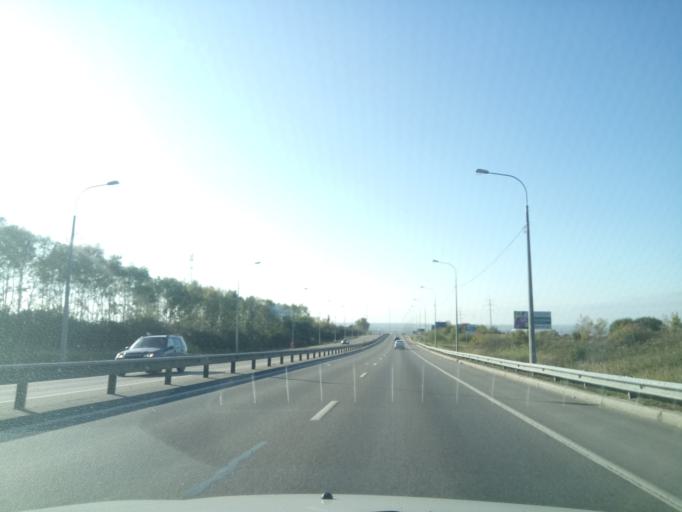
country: RU
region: Nizjnij Novgorod
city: Burevestnik
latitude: 56.1990
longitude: 43.9260
